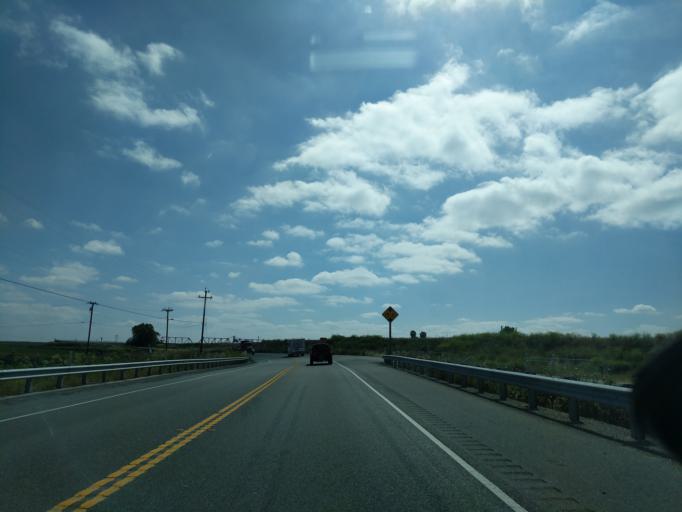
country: US
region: California
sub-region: Contra Costa County
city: Discovery Bay
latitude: 37.8901
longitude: -121.5802
